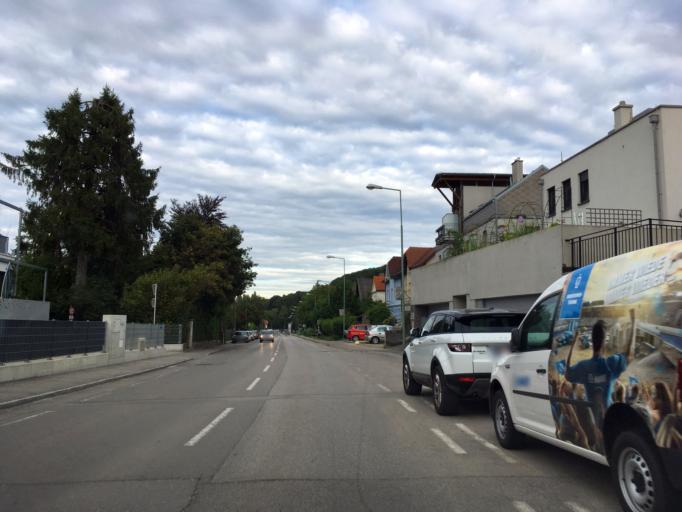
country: AT
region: Lower Austria
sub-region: Politischer Bezirk Tulln
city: Wordern
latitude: 48.3080
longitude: 16.2604
